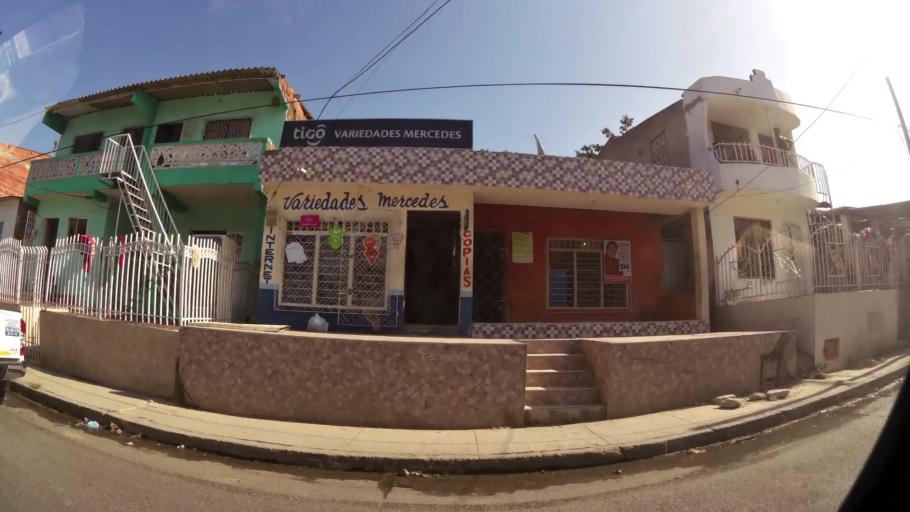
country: CO
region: Bolivar
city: Cartagena
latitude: 10.4289
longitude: -75.5189
